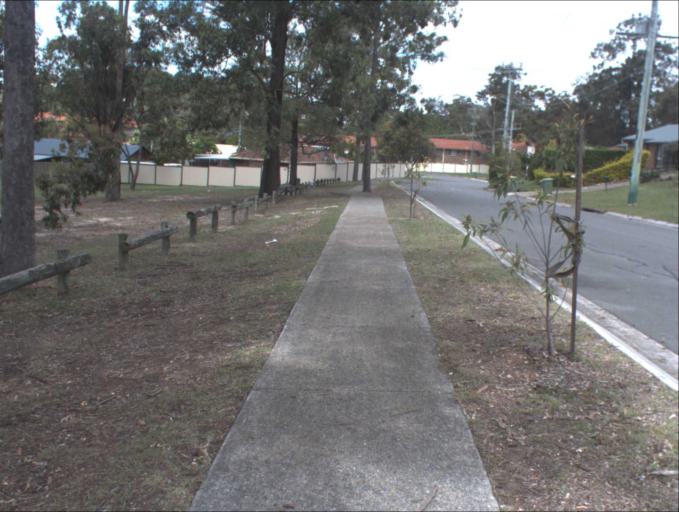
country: AU
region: Queensland
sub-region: Brisbane
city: Sunnybank Hills
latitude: -27.6660
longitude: 153.0298
